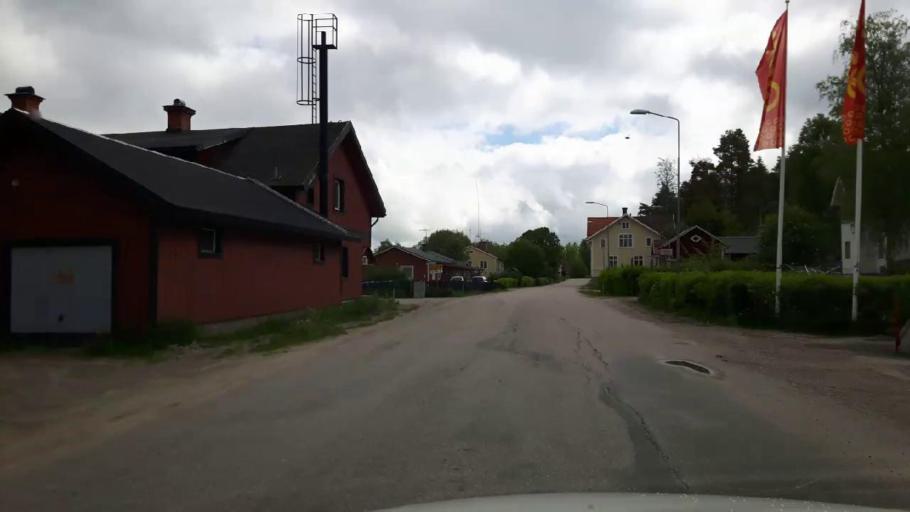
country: SE
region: Gaevleborg
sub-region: Ovanakers Kommun
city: Alfta
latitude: 61.3381
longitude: 15.9534
